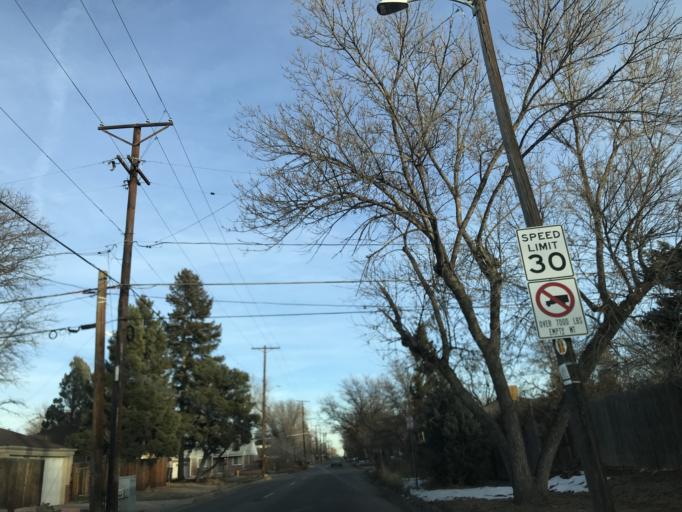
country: US
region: Colorado
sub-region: Arapahoe County
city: Glendale
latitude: 39.7387
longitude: -104.9078
